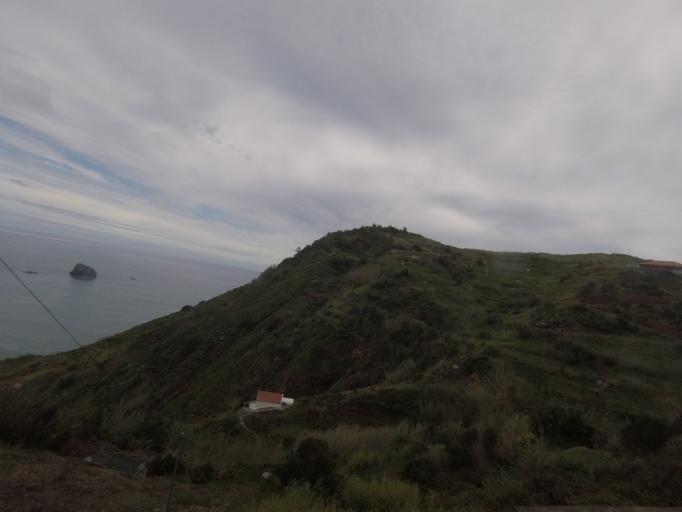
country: PT
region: Madeira
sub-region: Santana
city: Santana
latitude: 32.7656
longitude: -16.8173
